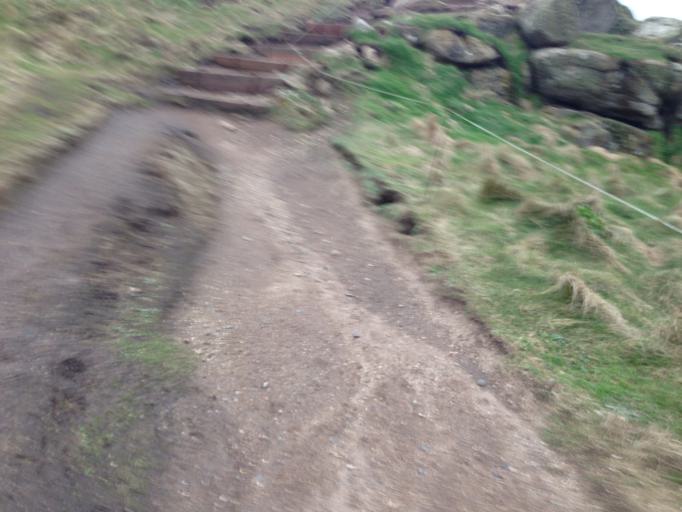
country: GB
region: England
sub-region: Cornwall
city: Sennen
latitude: 50.0634
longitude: -5.7131
